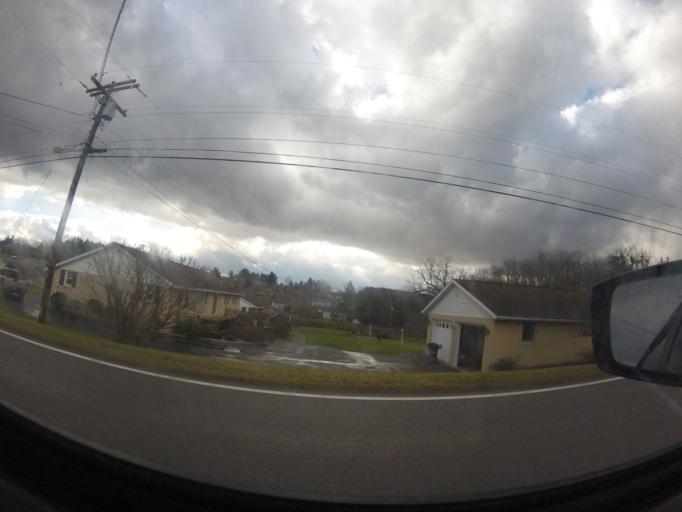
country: US
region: Maryland
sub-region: Garrett County
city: Mountain Lake Park
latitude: 39.4081
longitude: -79.3907
